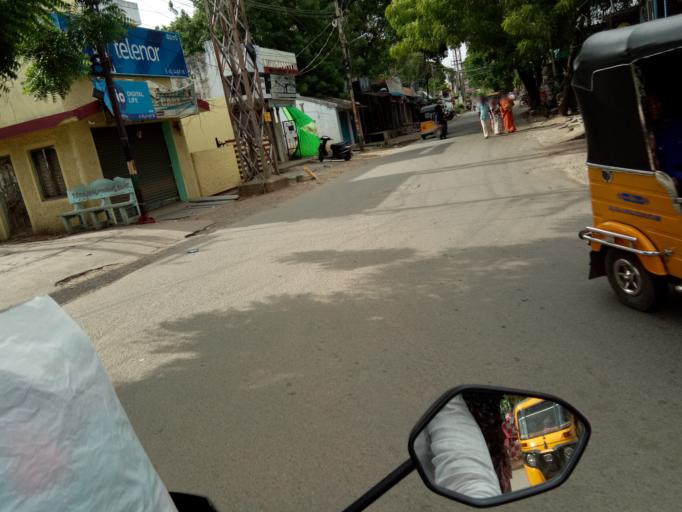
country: IN
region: Telangana
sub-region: Khammam
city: Khammam
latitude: 17.2411
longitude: 80.1419
